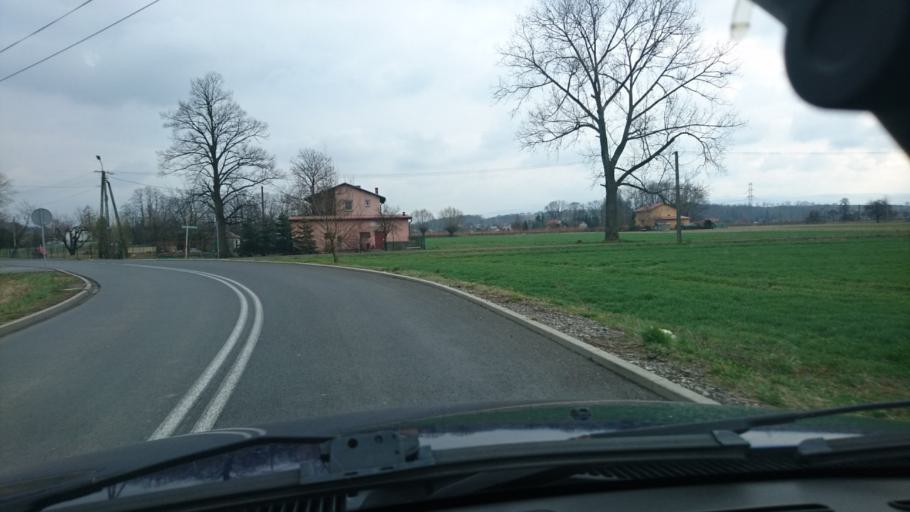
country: PL
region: Silesian Voivodeship
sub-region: Powiat bielski
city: Mazancowice
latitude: 49.8724
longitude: 18.9579
